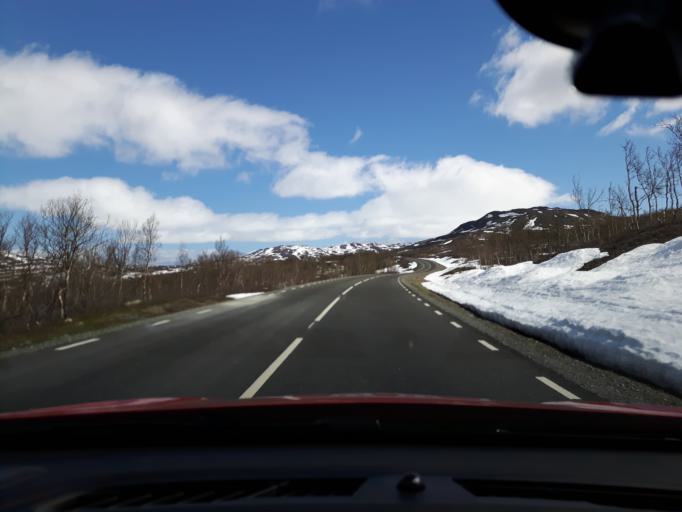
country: NO
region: Nordland
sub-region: Hattfjelldal
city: Hattfjelldal
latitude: 65.0052
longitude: 14.2580
